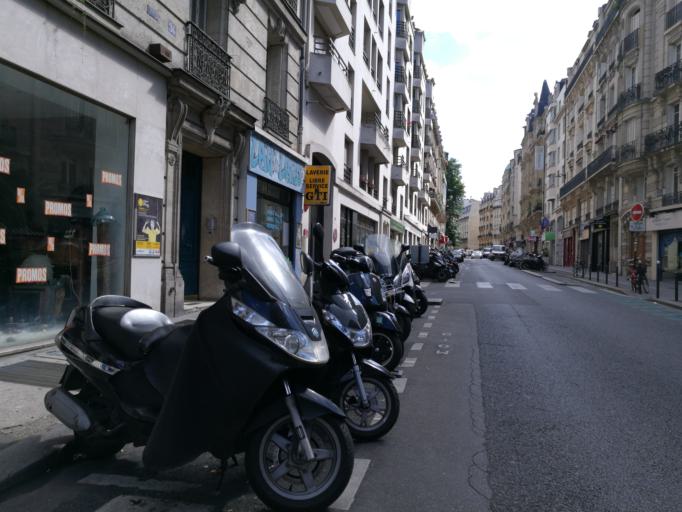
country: FR
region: Ile-de-France
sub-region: Paris
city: Saint-Ouen
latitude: 48.8896
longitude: 2.3337
